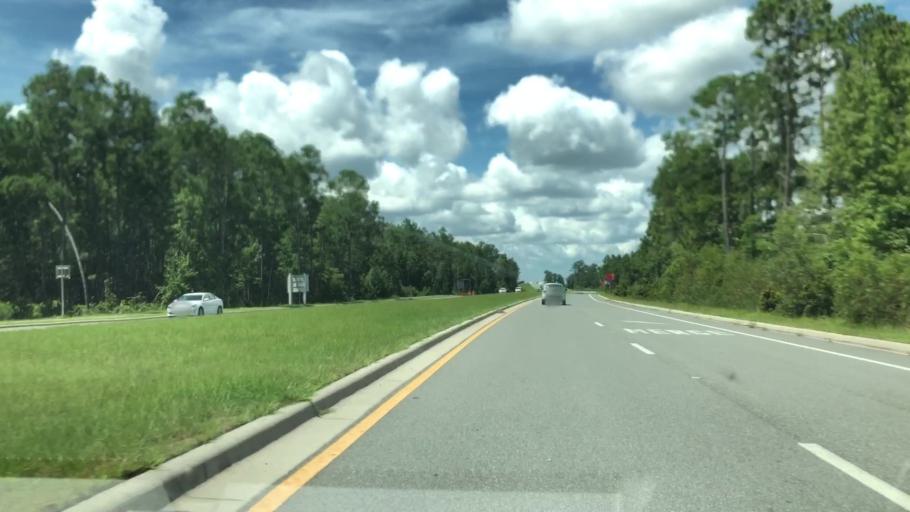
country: US
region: Florida
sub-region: Saint Johns County
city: Palm Valley
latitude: 30.0945
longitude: -81.4576
